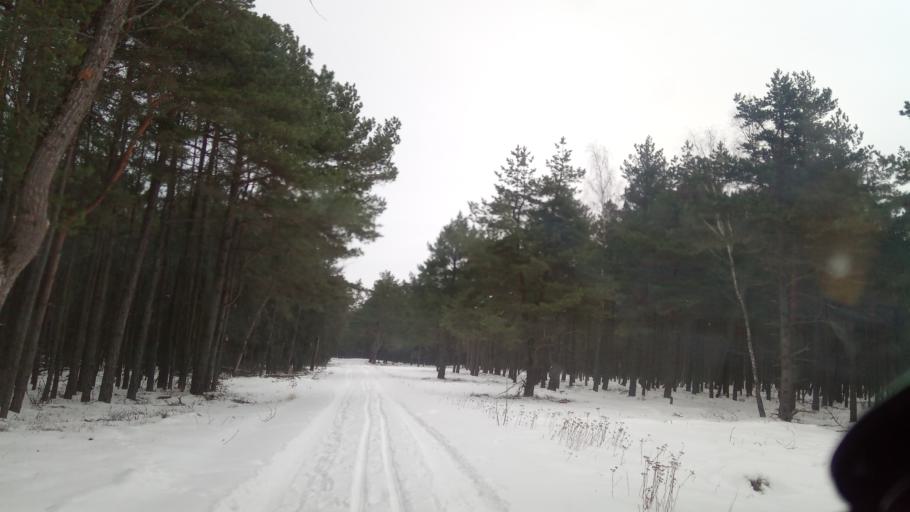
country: LT
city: Neringa
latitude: 55.4207
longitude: 21.0940
